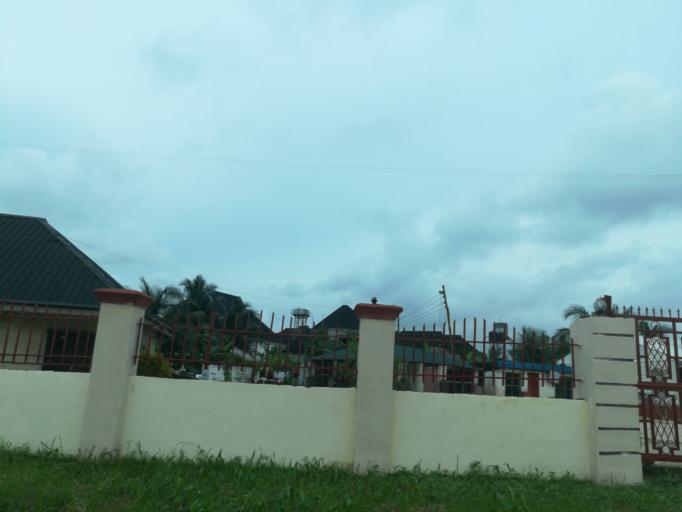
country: NG
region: Rivers
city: Port Harcourt
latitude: 4.8185
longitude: 6.9888
